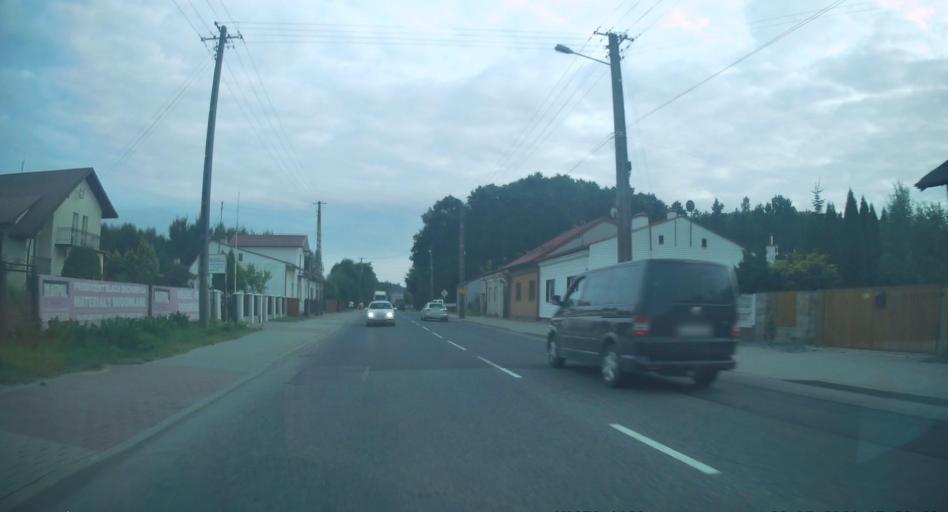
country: PL
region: Lodz Voivodeship
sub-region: Powiat radomszczanski
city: Kamiensk
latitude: 51.1908
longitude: 19.4979
